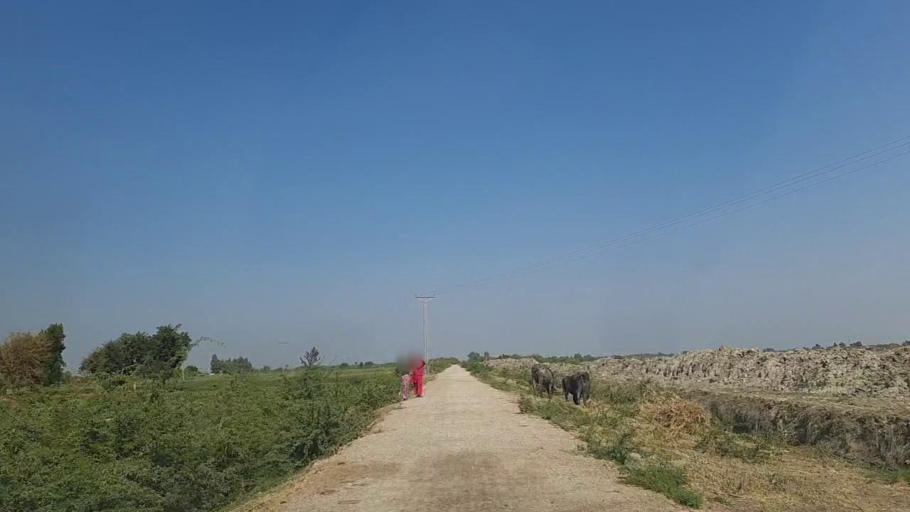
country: PK
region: Sindh
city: Digri
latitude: 25.1864
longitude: 69.1446
